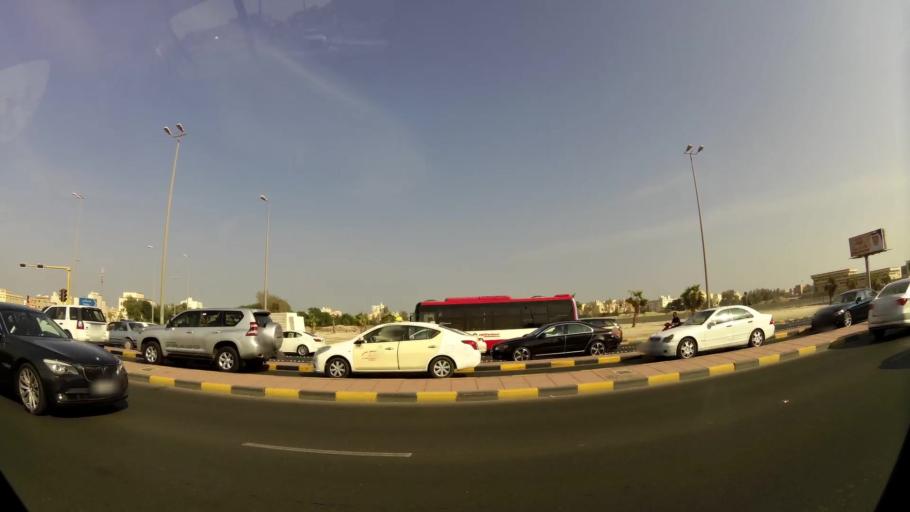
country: KW
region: Mubarak al Kabir
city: Mubarak al Kabir
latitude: 29.1753
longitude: 48.0997
